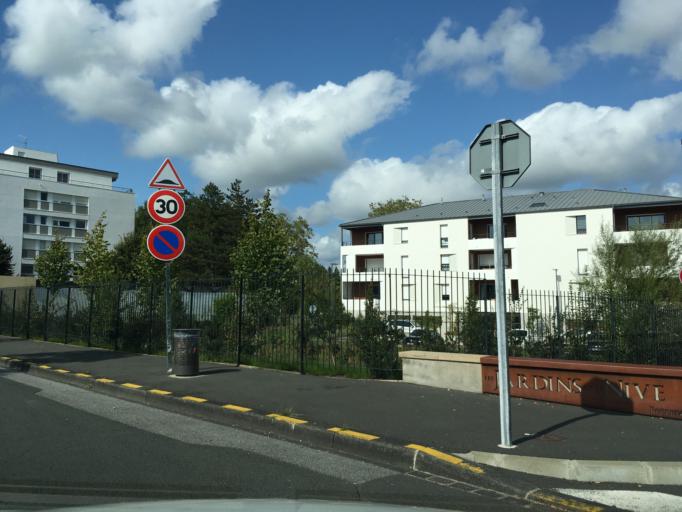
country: FR
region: Aquitaine
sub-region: Departement des Pyrenees-Atlantiques
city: Bayonne
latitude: 43.4826
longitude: -1.4737
